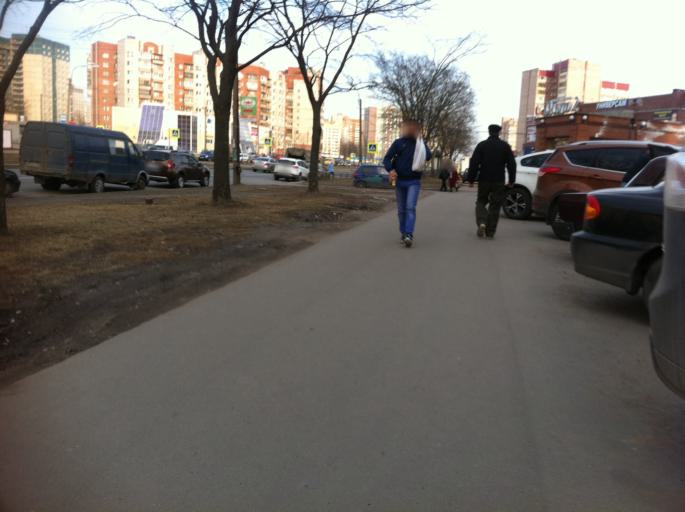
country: RU
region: St.-Petersburg
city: Uritsk
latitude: 59.8540
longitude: 30.1907
